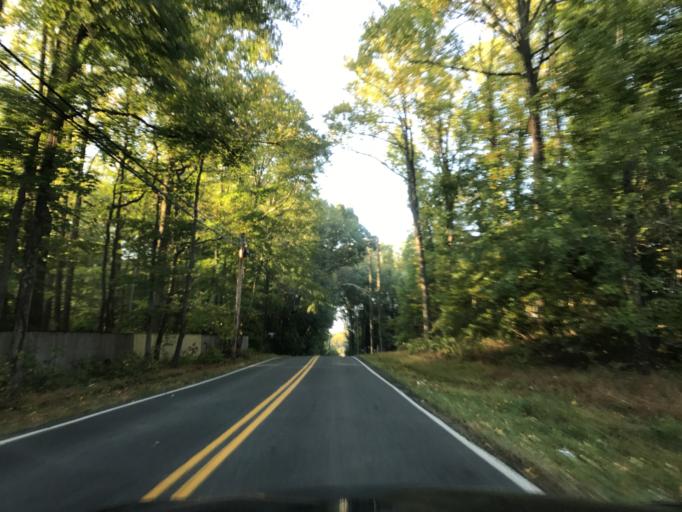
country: US
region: Maryland
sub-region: Anne Arundel County
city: Gambrills
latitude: 39.0317
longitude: -76.6515
